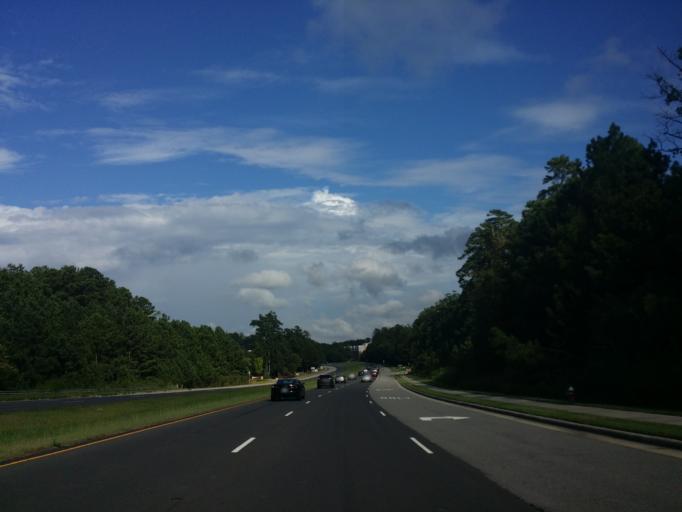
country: US
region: North Carolina
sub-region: Wake County
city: Morrisville
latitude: 35.9185
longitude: -78.7983
